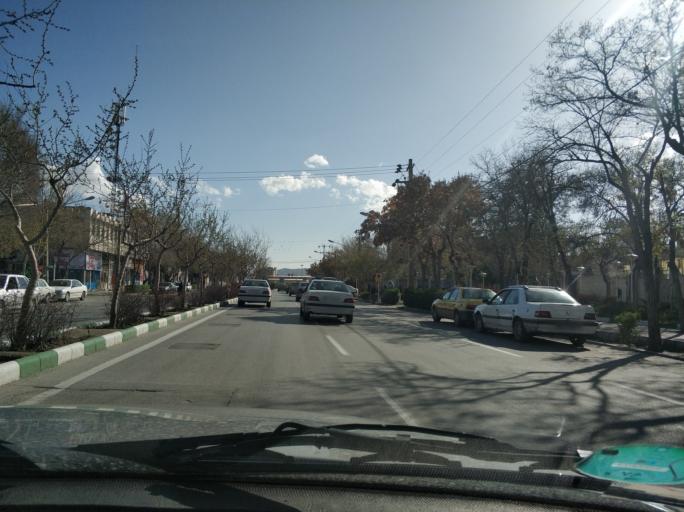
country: IR
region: Razavi Khorasan
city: Mashhad
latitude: 36.3124
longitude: 59.6251
